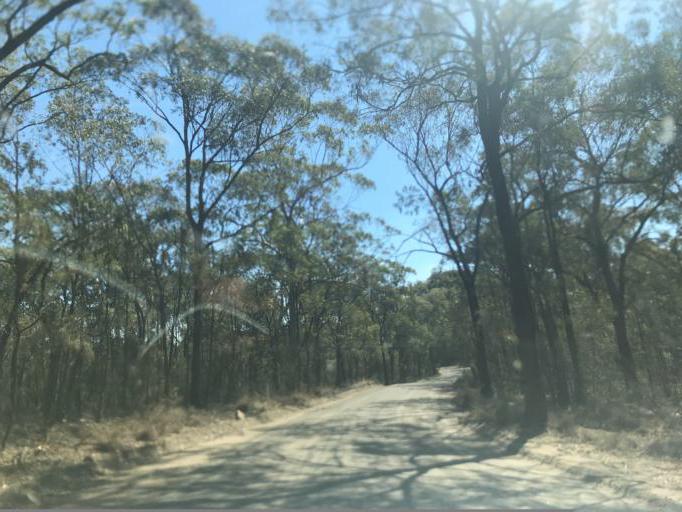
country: AU
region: New South Wales
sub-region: Hawkesbury
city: Pitt Town
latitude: -33.4641
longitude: 150.8393
